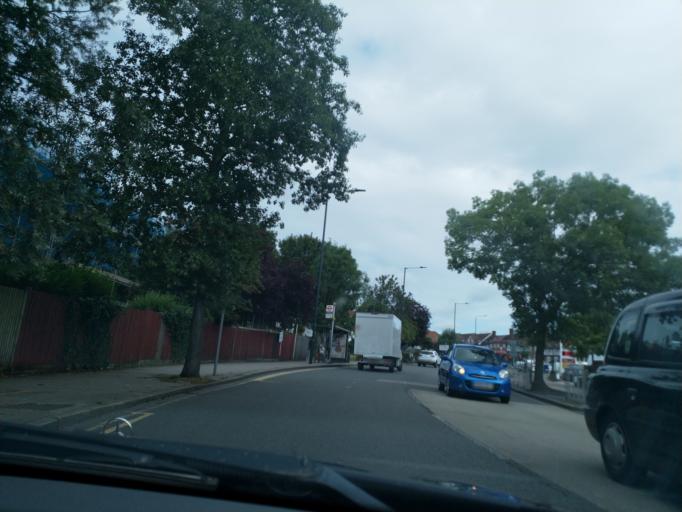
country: GB
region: England
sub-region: Greater London
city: Harrow on the Hill
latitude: 51.5604
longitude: -0.3195
